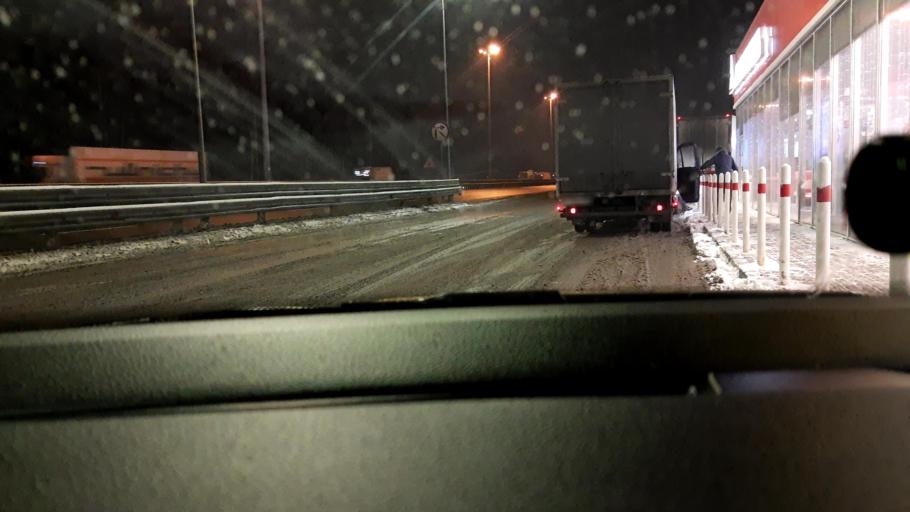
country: RU
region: Moskovskaya
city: Noginsk
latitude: 55.8422
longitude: 38.4799
